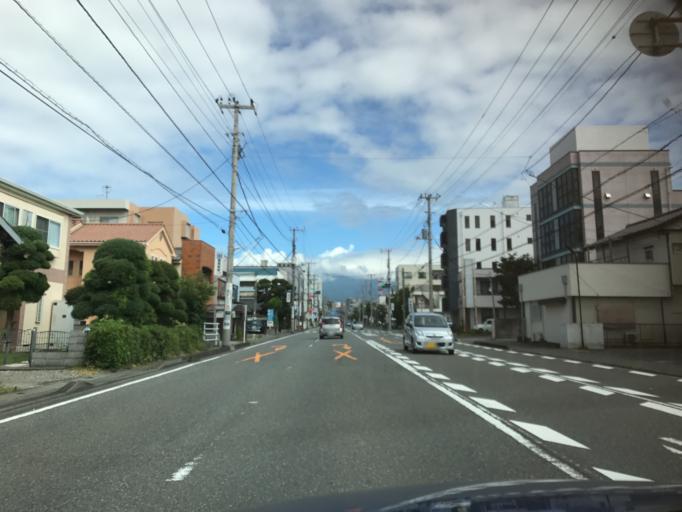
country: JP
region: Shizuoka
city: Numazu
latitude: 35.0919
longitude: 138.8655
